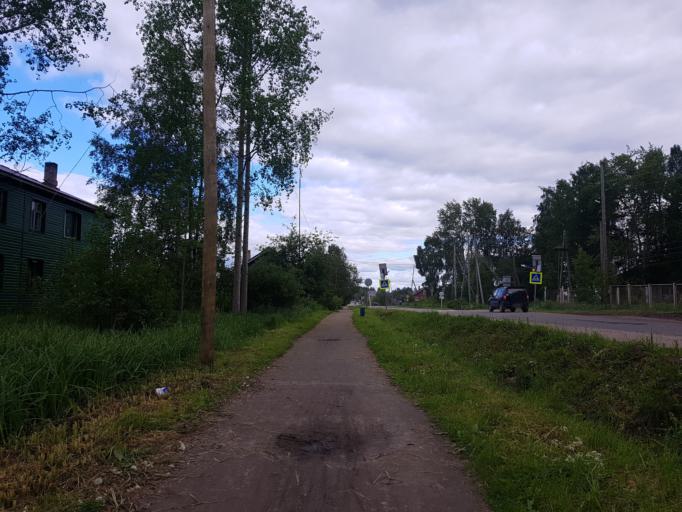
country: RU
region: Republic of Karelia
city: Kalevala
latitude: 65.2023
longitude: 31.1753
